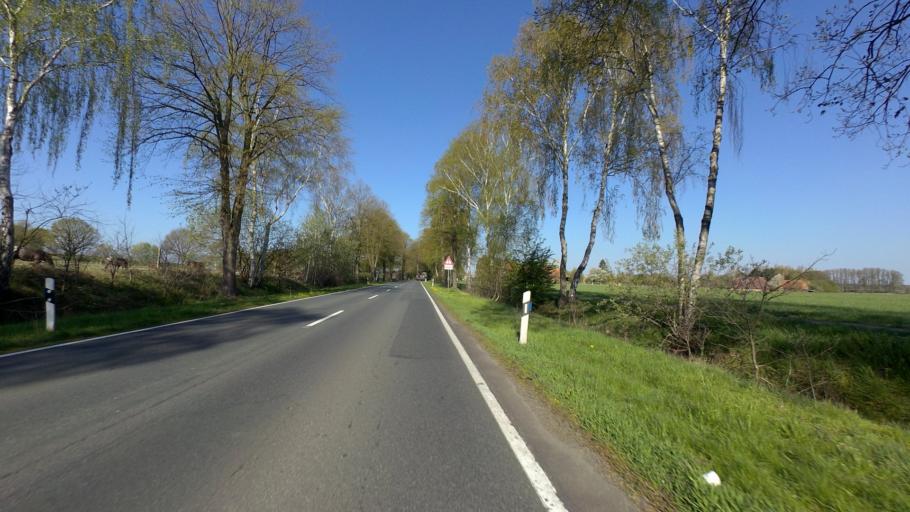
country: DE
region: Lower Saxony
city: Steimbke
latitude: 52.6508
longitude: 9.4208
